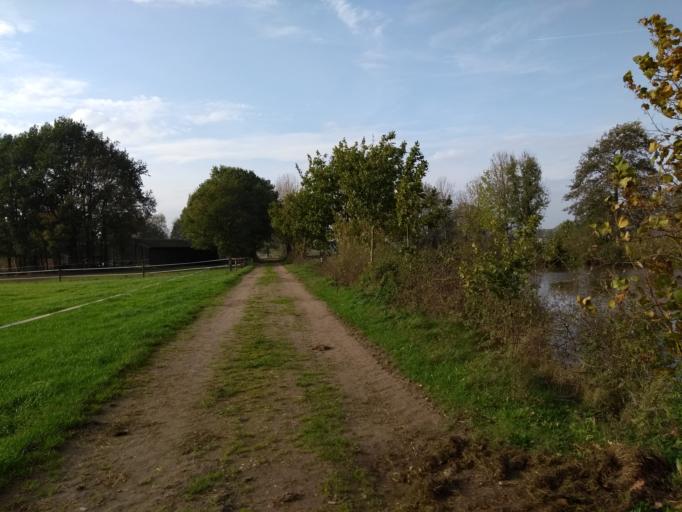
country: NL
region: Overijssel
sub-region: Gemeente Almelo
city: Almelo
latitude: 52.3880
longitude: 6.6740
